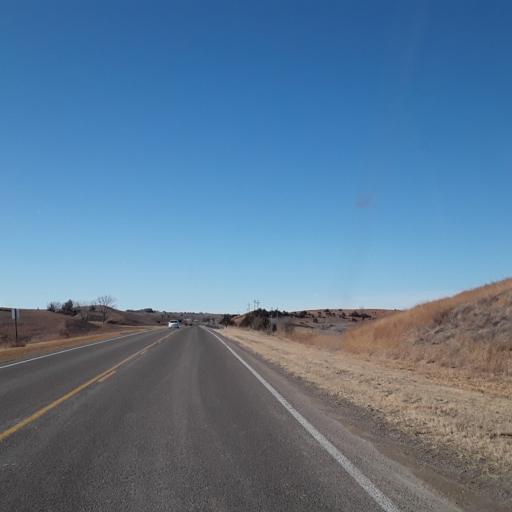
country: US
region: Nebraska
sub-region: Frontier County
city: Stockville
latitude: 40.6301
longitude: -100.5540
